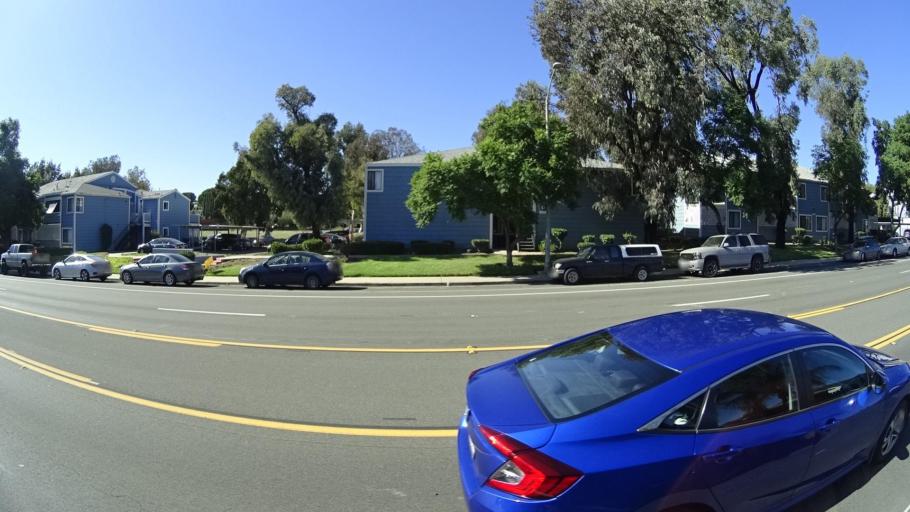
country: US
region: California
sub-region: San Diego County
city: Rancho San Diego
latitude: 32.7315
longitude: -116.9596
